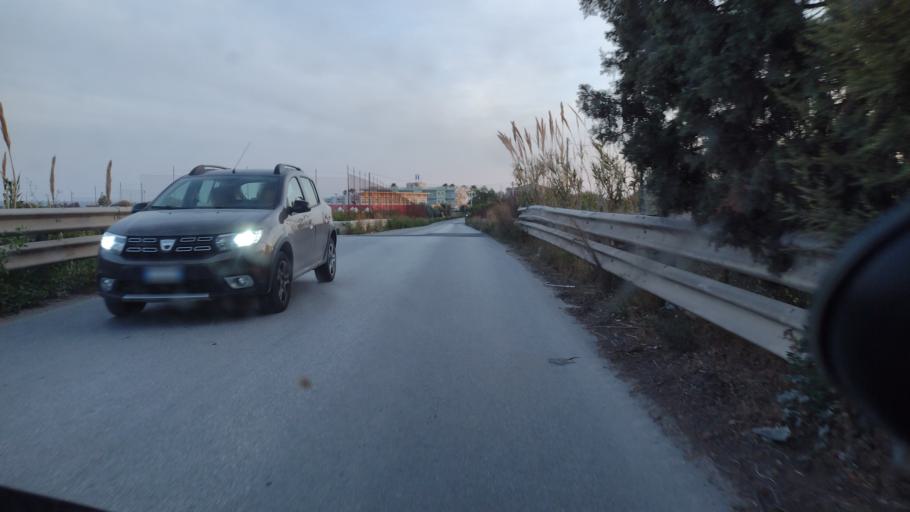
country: IT
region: Sicily
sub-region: Provincia di Siracusa
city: Avola
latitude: 36.8976
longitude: 15.1342
